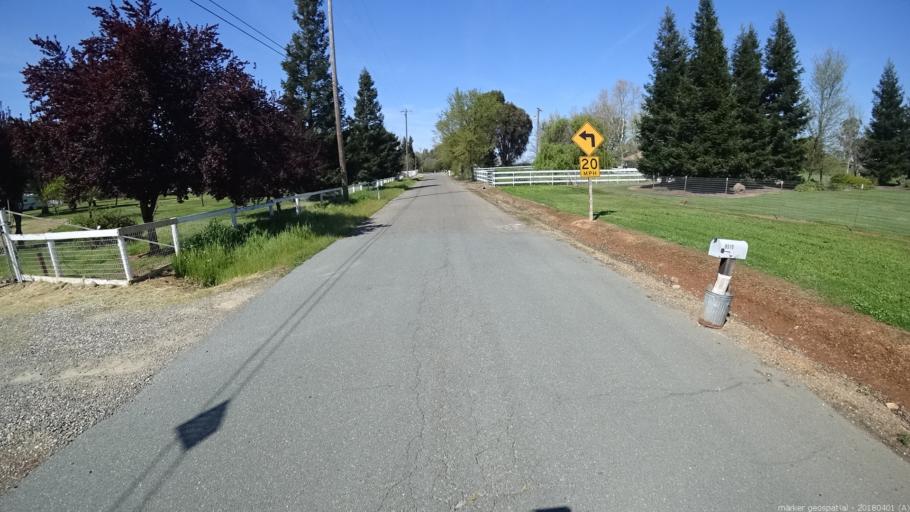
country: US
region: California
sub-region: Sacramento County
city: Wilton
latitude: 38.4118
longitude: -121.2522
